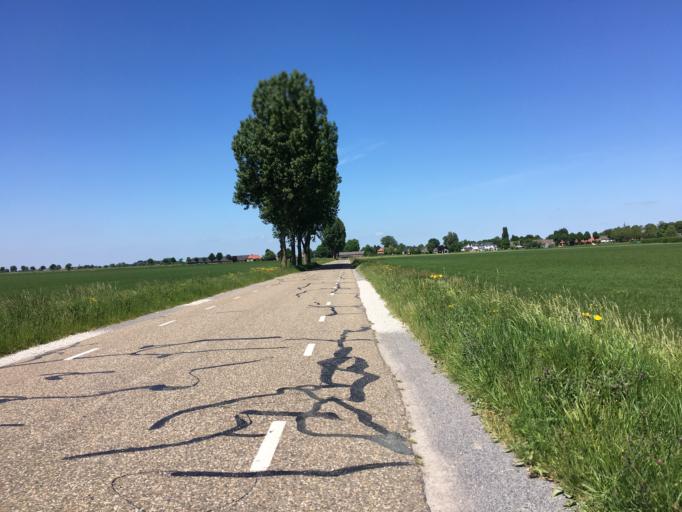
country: NL
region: Gelderland
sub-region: Gemeente Maasdriel
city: Hedel
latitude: 51.7303
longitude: 5.2338
